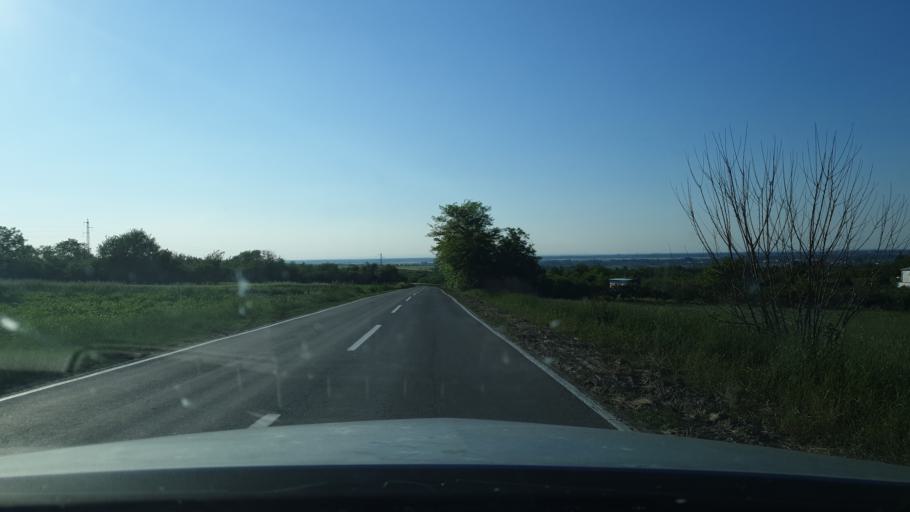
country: RS
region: Central Serbia
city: Sremcica
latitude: 44.7063
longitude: 20.3702
